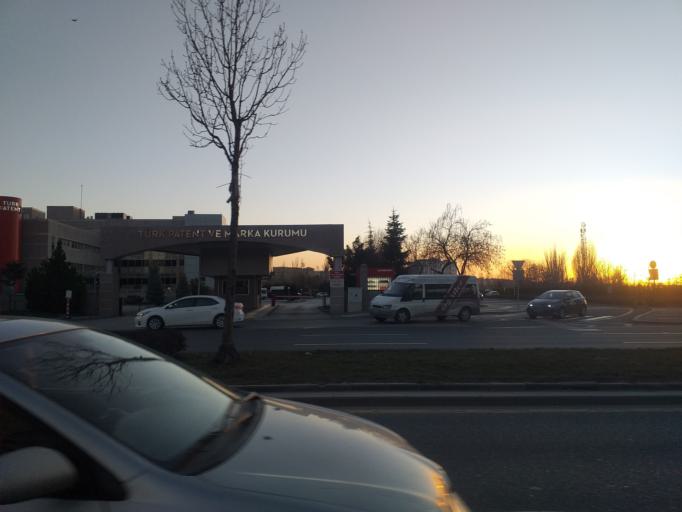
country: TR
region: Ankara
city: Ankara
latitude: 39.9480
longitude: 32.8281
